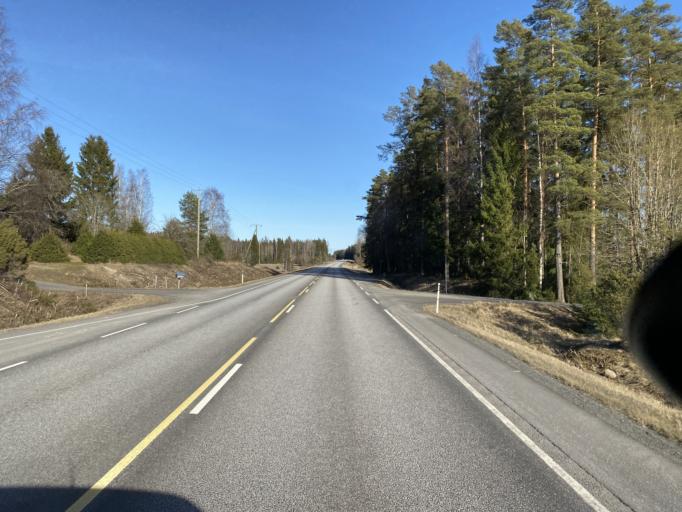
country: FI
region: Satakunta
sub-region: Rauma
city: Kiukainen
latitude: 61.1314
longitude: 21.9990
